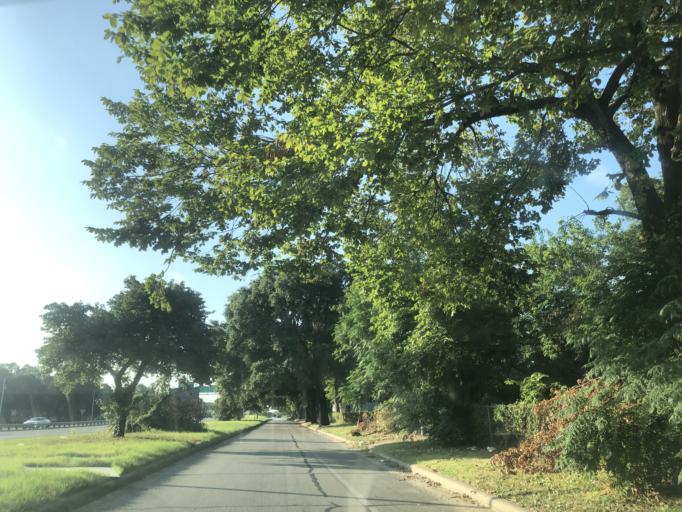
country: US
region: Texas
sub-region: Dallas County
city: Dallas
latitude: 32.7611
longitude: -96.7715
